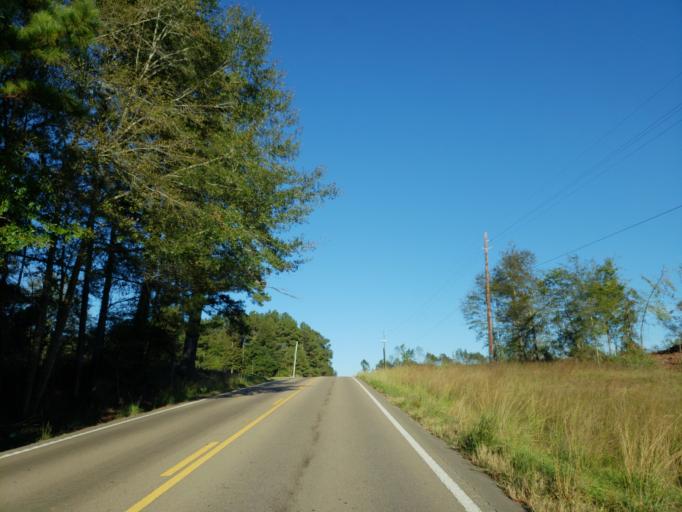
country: US
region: Mississippi
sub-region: Perry County
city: Richton
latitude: 31.3605
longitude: -88.8992
